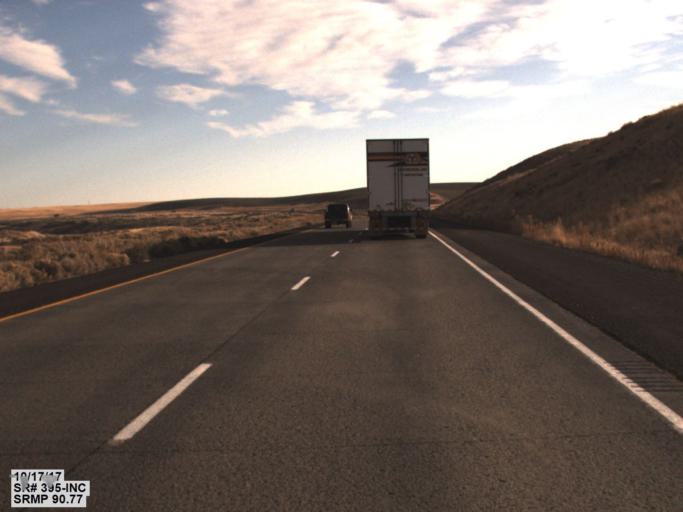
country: US
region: Washington
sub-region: Adams County
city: Ritzville
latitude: 47.0496
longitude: -118.4342
